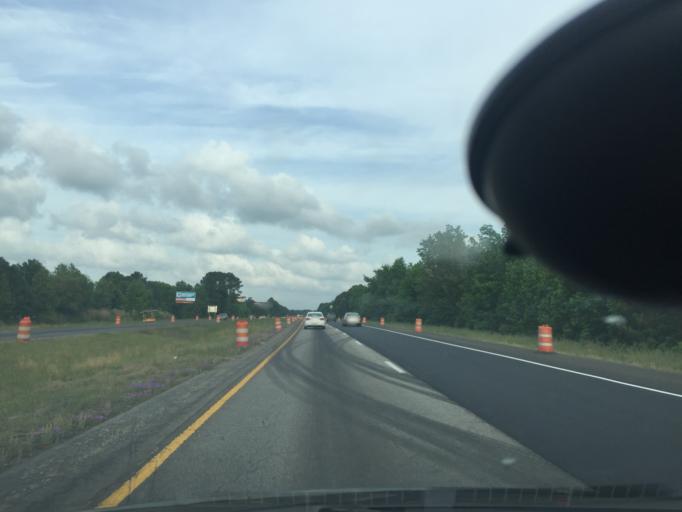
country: US
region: Georgia
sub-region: Chatham County
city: Georgetown
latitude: 32.0021
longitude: -81.2677
